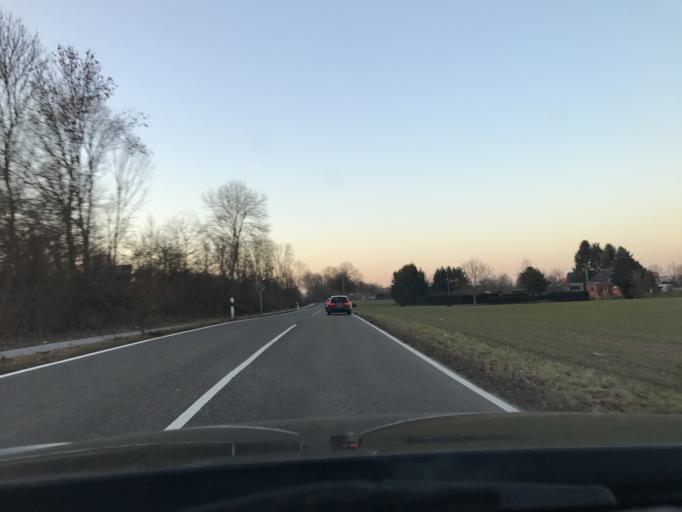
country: DE
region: North Rhine-Westphalia
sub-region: Regierungsbezirk Dusseldorf
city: Meerbusch
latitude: 51.3047
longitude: 6.6368
